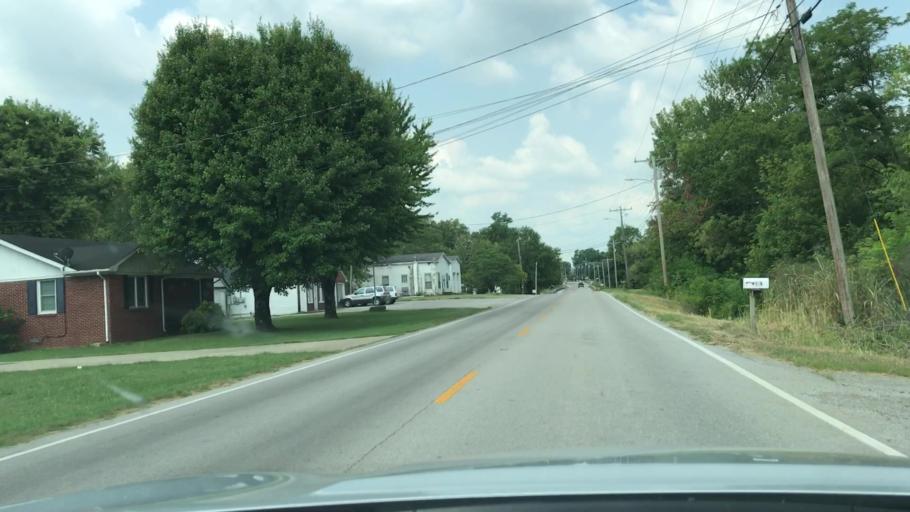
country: US
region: Kentucky
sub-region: Todd County
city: Elkton
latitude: 36.8078
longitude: -87.1424
